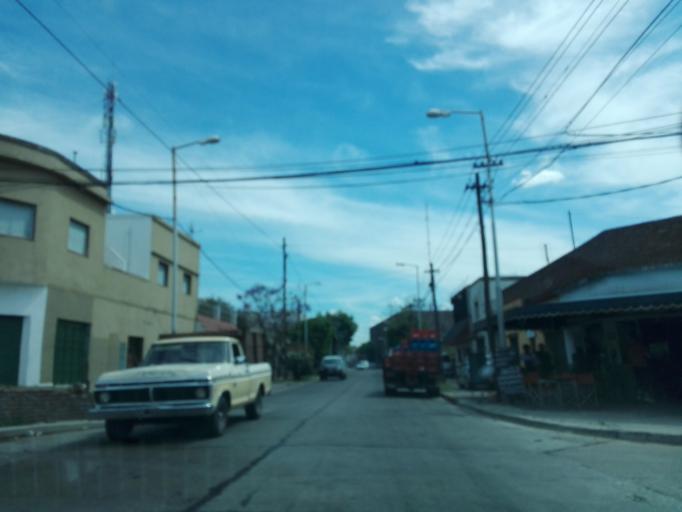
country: AR
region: Buenos Aires
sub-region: Partido de Avellaneda
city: Avellaneda
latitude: -34.6922
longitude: -58.3557
